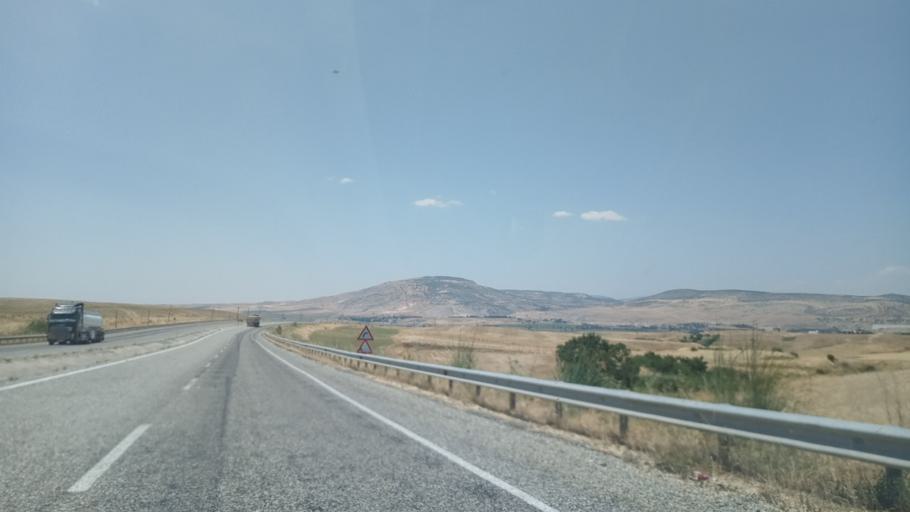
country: TR
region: Batman
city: Bekirhan
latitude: 38.1345
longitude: 41.2470
